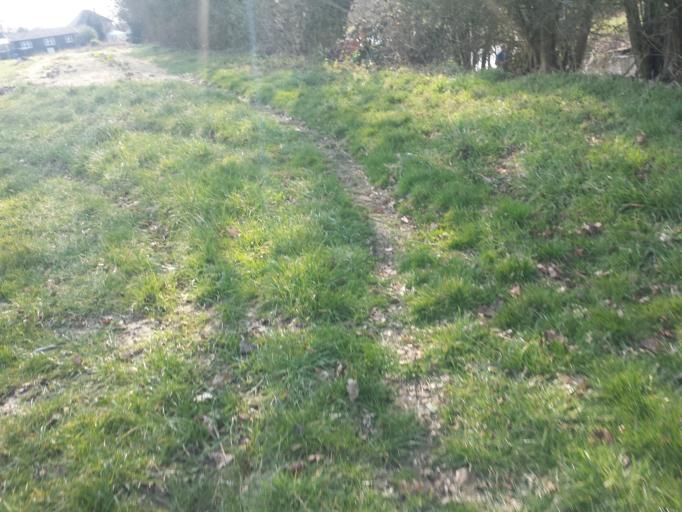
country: GB
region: England
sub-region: Essex
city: Little Clacton
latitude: 51.8833
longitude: 1.1595
